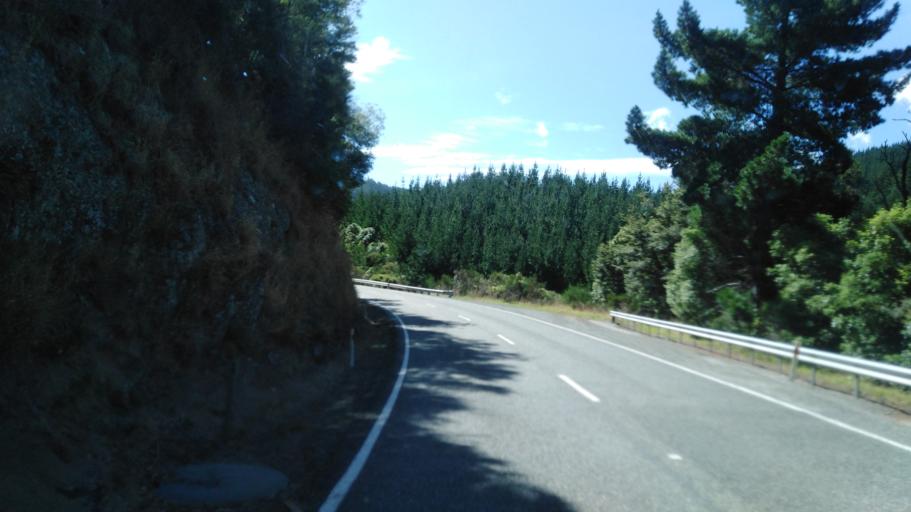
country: NZ
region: Nelson
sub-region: Nelson City
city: Nelson
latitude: -41.1722
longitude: 173.5629
